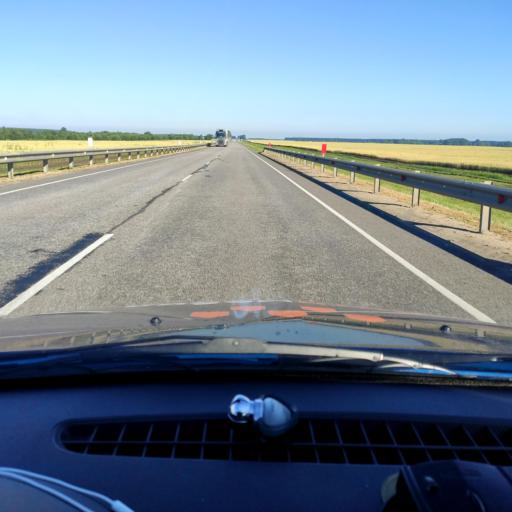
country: RU
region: Orjol
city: Pokrovskoye
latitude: 52.6236
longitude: 36.7224
